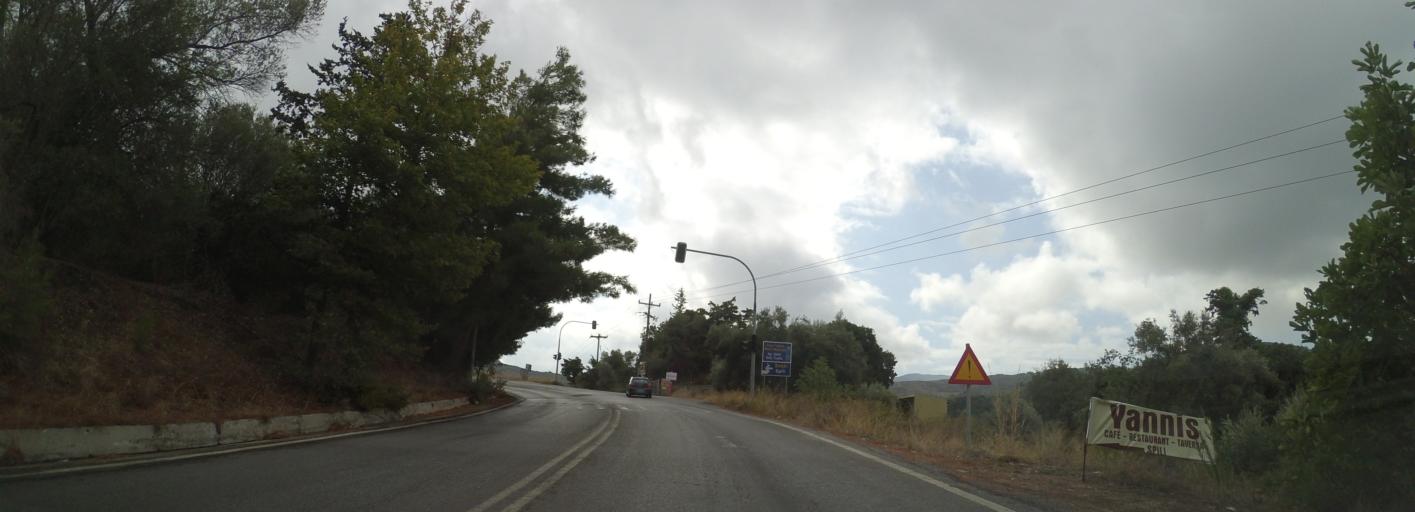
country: GR
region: Crete
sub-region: Nomos Rethymnis
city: Agia Foteini
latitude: 35.2198
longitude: 24.5276
